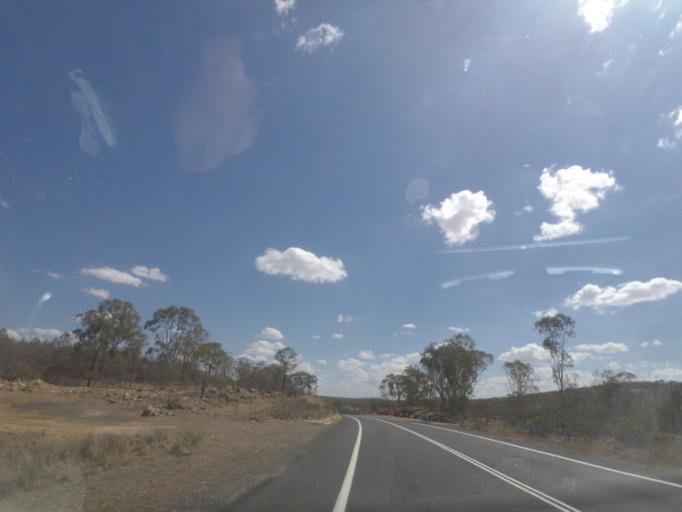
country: AU
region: Queensland
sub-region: Southern Downs
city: Warwick
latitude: -28.2206
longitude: 151.5550
